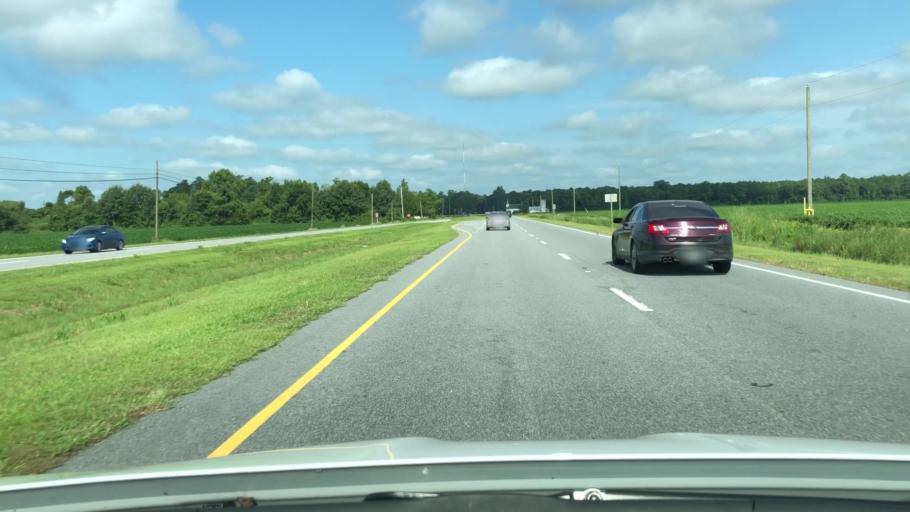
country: US
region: North Carolina
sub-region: Perquimans County
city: Hertford
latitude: 36.2105
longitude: -76.4221
